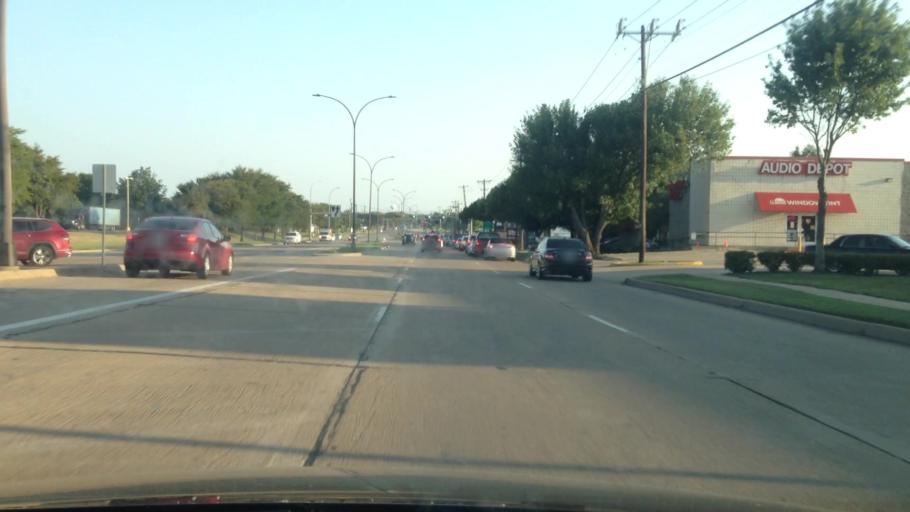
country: US
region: Texas
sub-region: Tarrant County
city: Dalworthington Gardens
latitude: 32.6760
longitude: -97.1151
